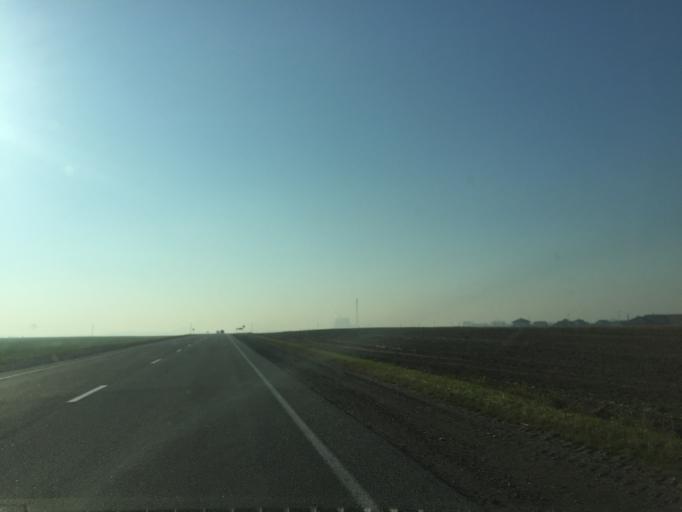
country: BY
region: Gomel
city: Kastsyukowka
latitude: 52.4819
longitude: 30.8205
